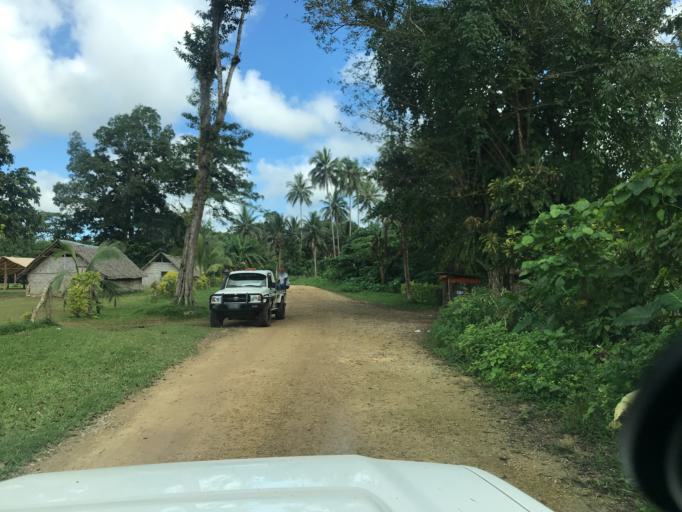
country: VU
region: Sanma
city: Luganville
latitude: -15.4727
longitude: 167.0792
